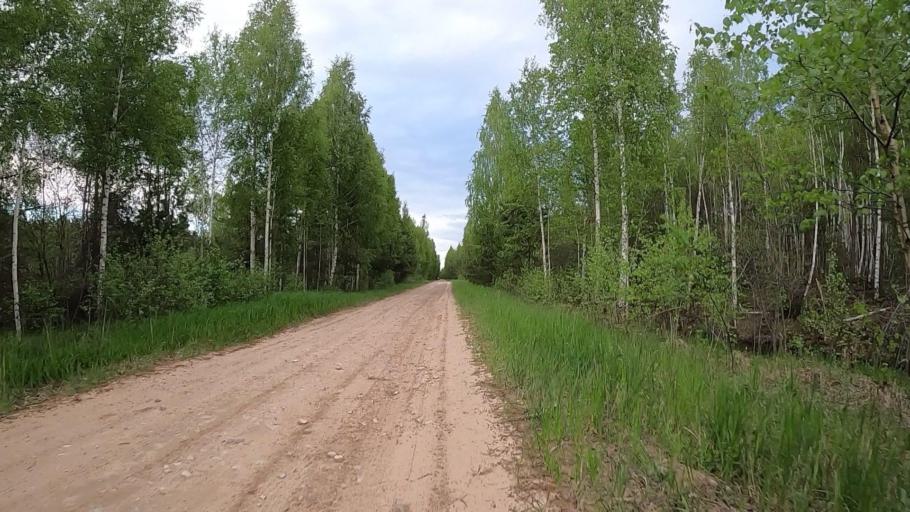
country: LV
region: Olaine
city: Olaine
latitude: 56.8415
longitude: 23.9311
